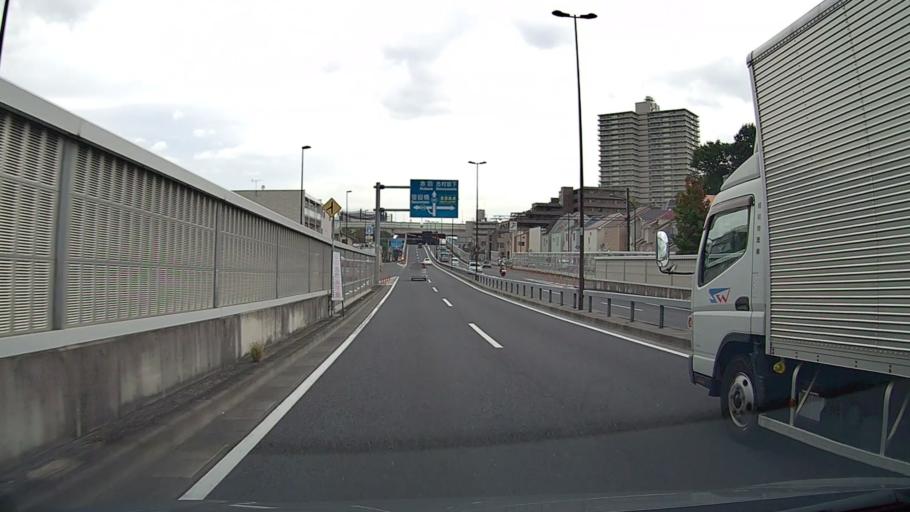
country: JP
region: Saitama
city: Shimotoda
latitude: 35.7742
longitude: 139.6742
